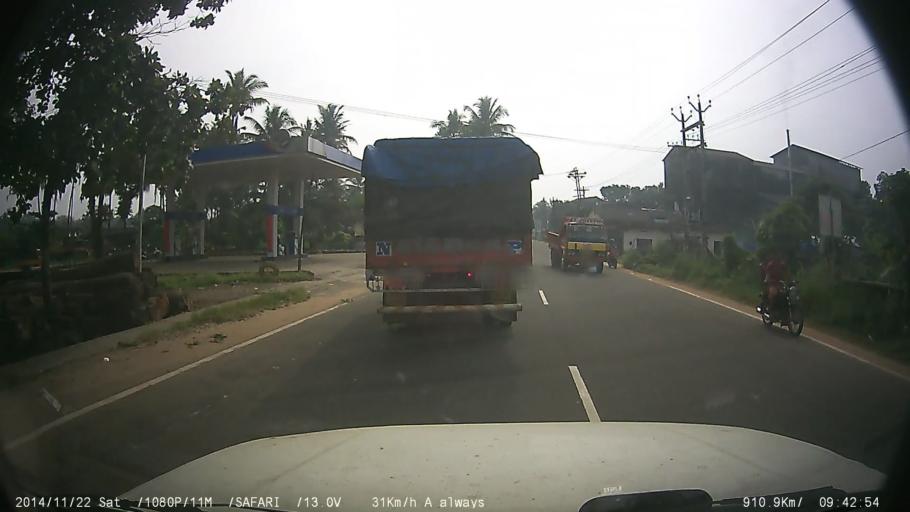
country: IN
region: Kerala
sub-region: Ernakulam
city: Perumpavur
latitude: 10.1493
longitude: 76.4550
